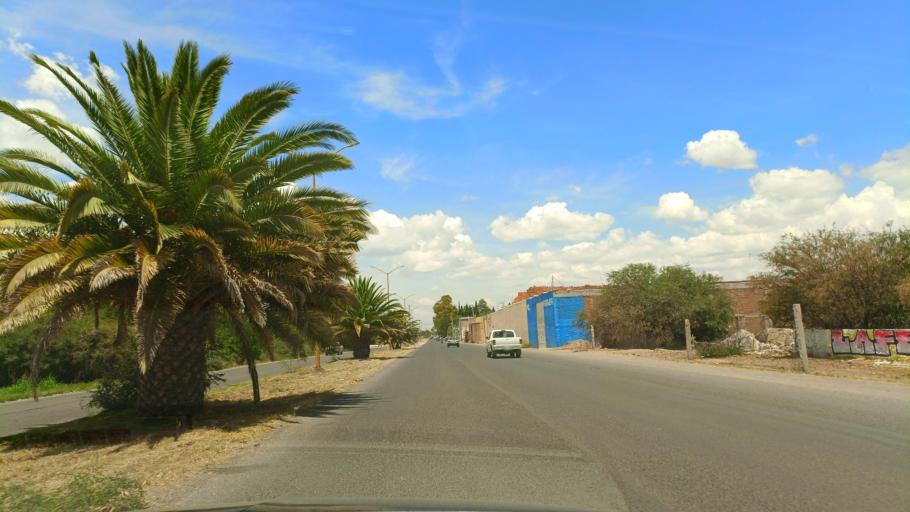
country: MX
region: Guanajuato
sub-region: San Luis de la Paz
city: San Ignacio
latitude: 21.2914
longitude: -100.5442
